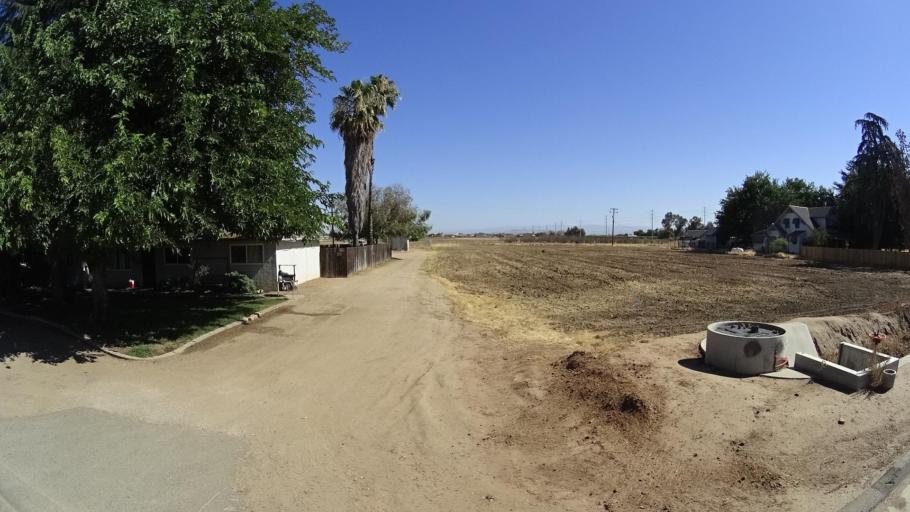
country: US
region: California
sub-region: Fresno County
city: Sunnyside
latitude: 36.7611
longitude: -119.6797
